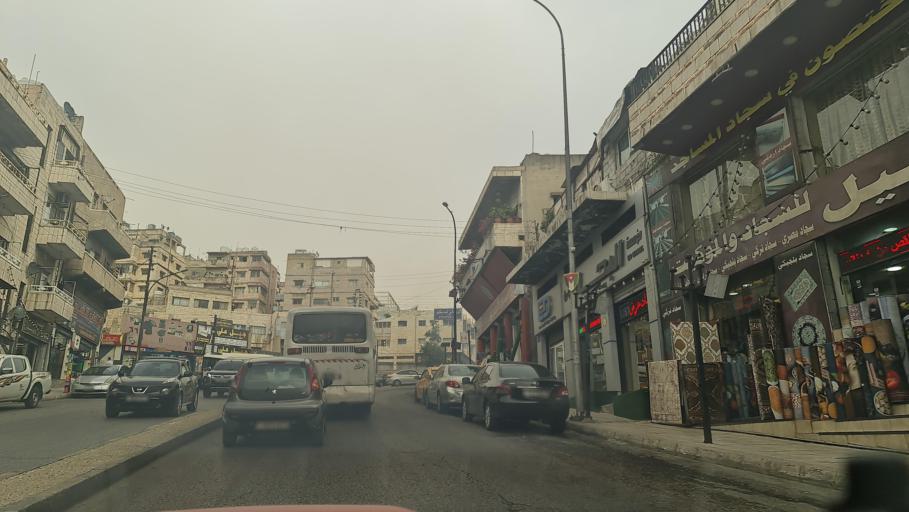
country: JO
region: Amman
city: Amman
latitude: 31.9365
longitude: 35.9309
